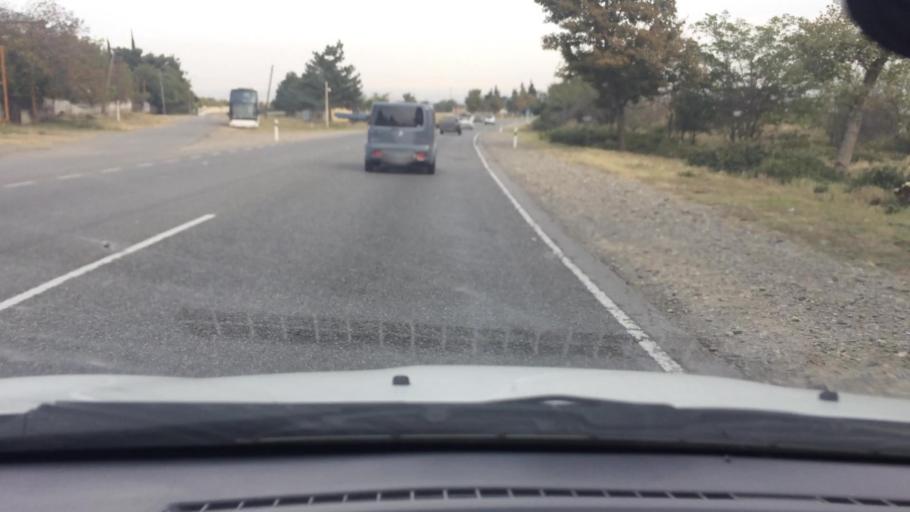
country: GE
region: T'bilisi
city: Tbilisi
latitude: 41.6437
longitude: 44.8499
